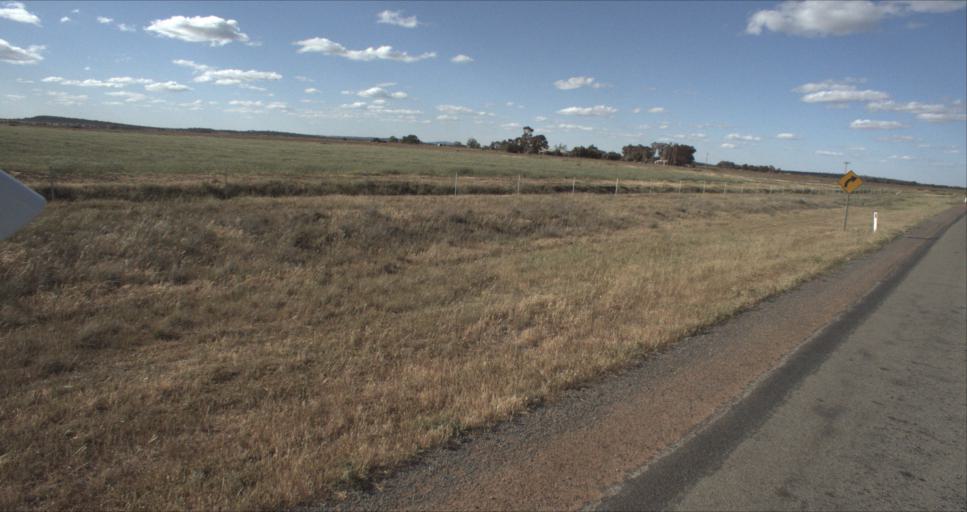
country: AU
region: New South Wales
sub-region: Leeton
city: Leeton
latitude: -34.4560
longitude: 146.2736
